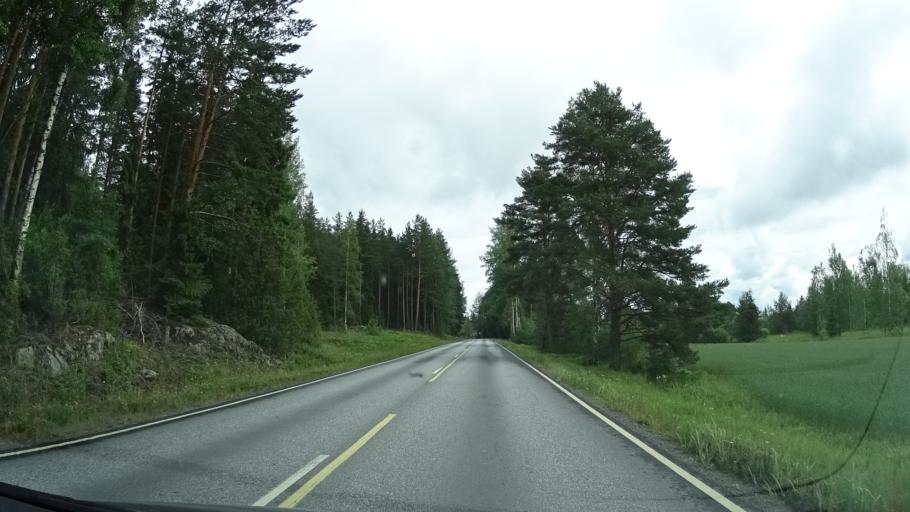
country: FI
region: Haeme
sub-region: Forssa
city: Humppila
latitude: 61.0942
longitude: 23.3678
